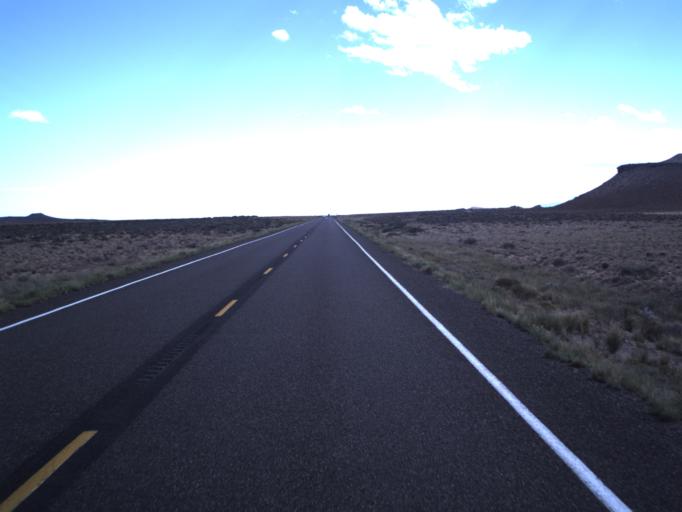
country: US
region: Utah
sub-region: Emery County
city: Ferron
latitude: 38.2876
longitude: -110.6647
